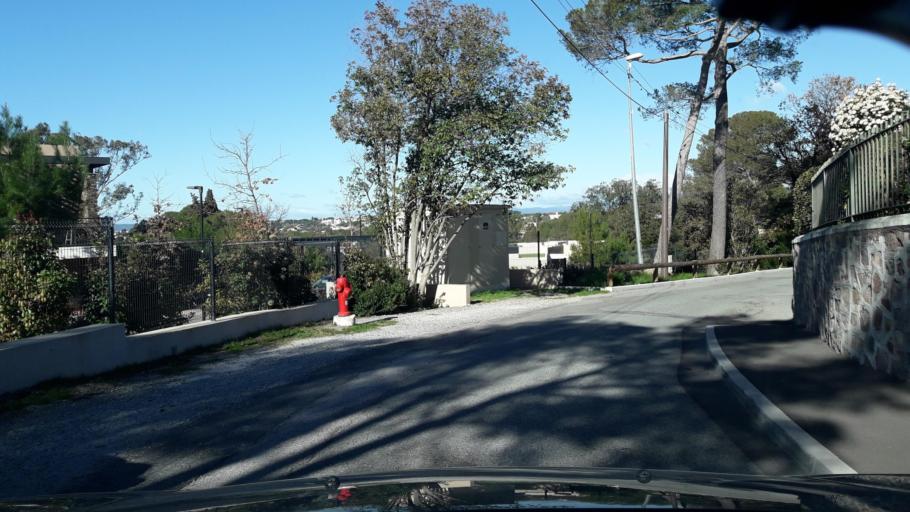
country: FR
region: Provence-Alpes-Cote d'Azur
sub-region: Departement du Var
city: Saint-Raphael
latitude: 43.4411
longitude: 6.7763
